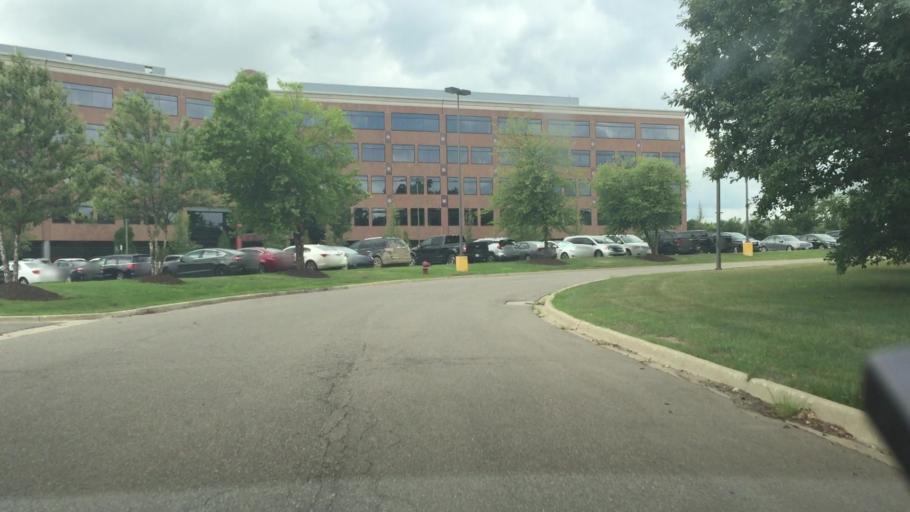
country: US
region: Michigan
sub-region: Oakland County
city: Auburn Hills
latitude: 42.6697
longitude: -83.2382
